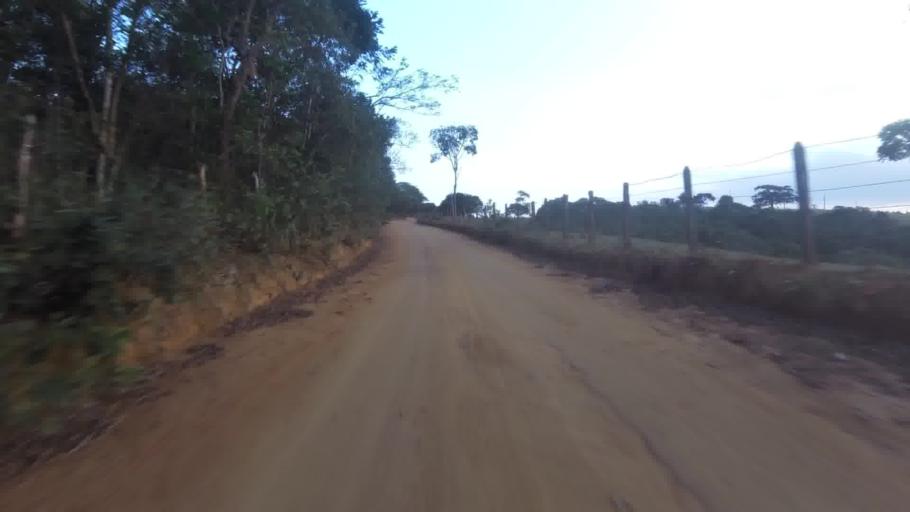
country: BR
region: Espirito Santo
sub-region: Guarapari
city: Guarapari
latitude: -20.6984
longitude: -40.5737
